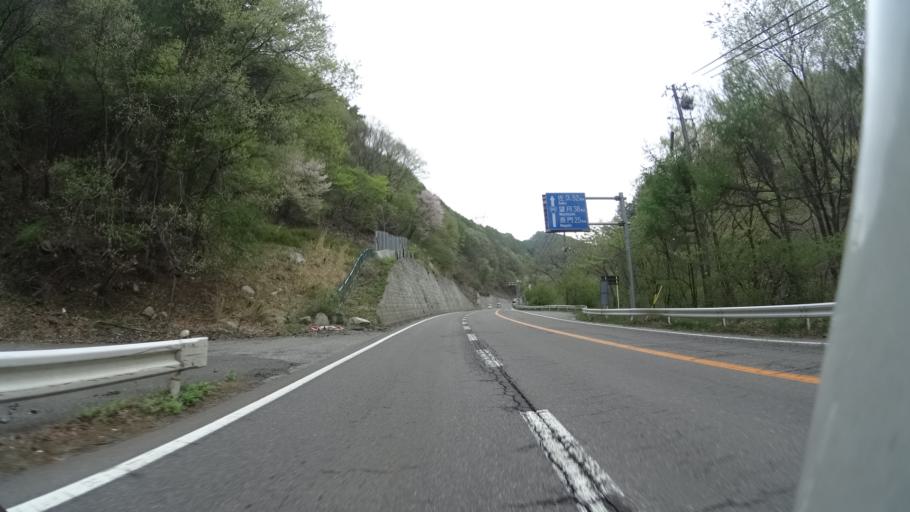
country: JP
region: Nagano
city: Suwa
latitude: 36.1259
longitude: 138.1081
